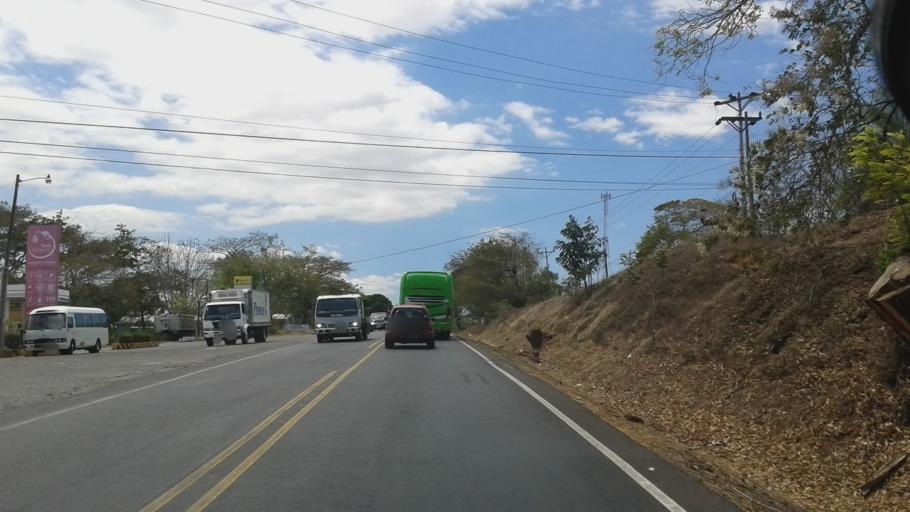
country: CR
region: Puntarenas
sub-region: Canton Central de Puntarenas
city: Puntarenas
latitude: 10.1106
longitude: -84.8889
